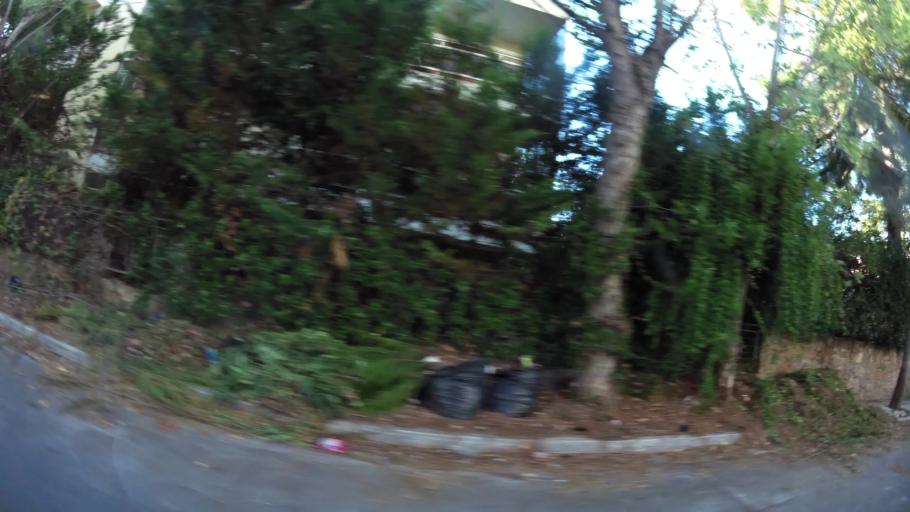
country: GR
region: Attica
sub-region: Nomarchia Athinas
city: Nea Erythraia
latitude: 38.0966
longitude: 23.8271
